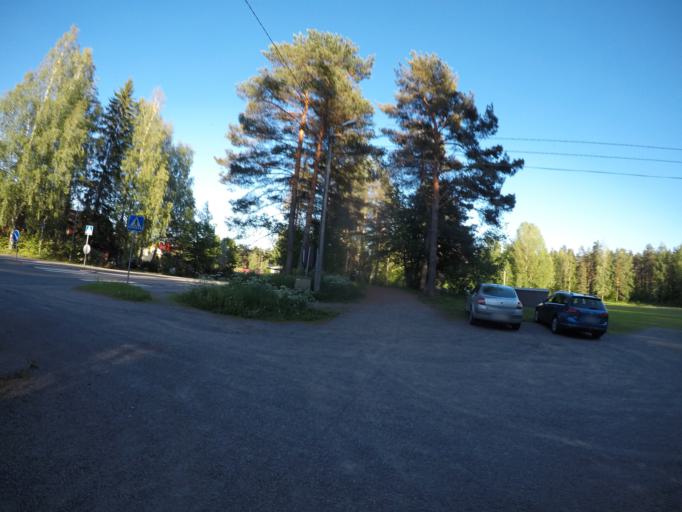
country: FI
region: Haeme
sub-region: Haemeenlinna
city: Haemeenlinna
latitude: 60.9817
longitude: 24.4536
